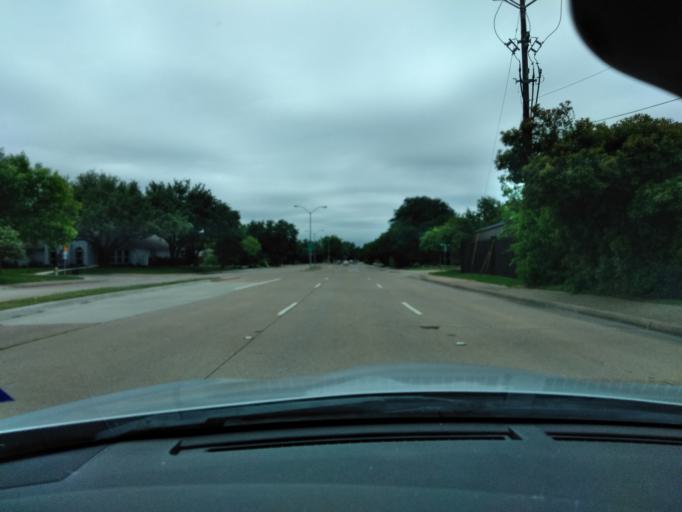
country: US
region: Texas
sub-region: Dallas County
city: Addison
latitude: 32.9737
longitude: -96.7840
